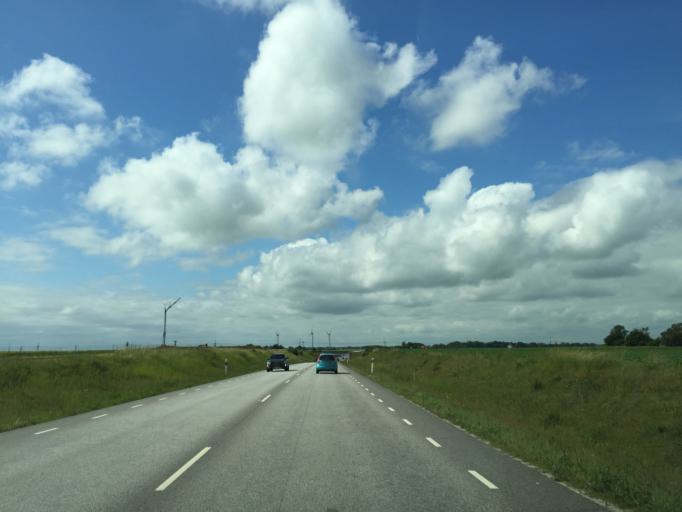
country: SE
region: Skane
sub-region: Staffanstorps Kommun
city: Hjaerup
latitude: 55.6831
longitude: 13.1614
